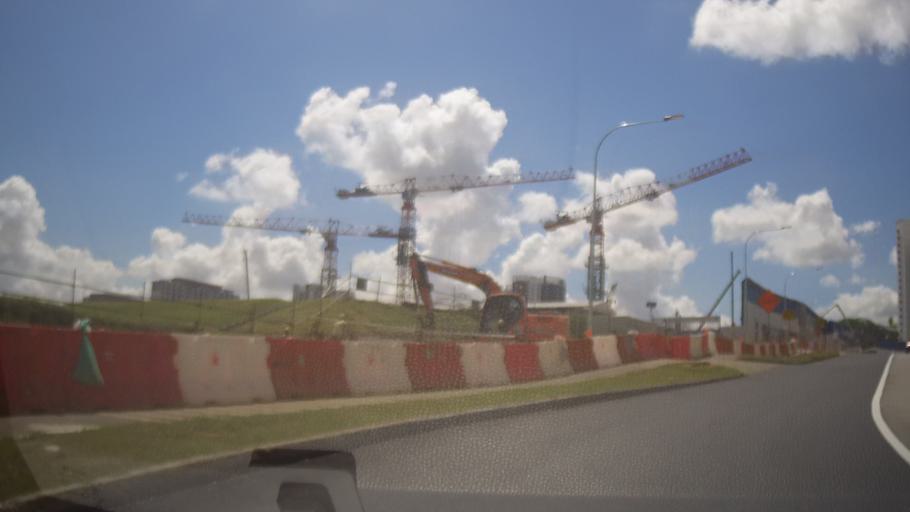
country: MY
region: Johor
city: Johor Bahru
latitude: 1.4364
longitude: 103.7725
